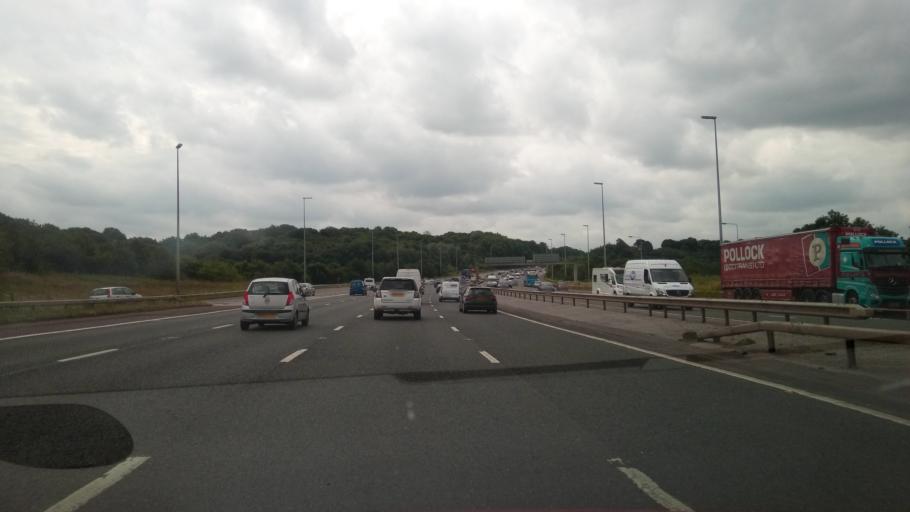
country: GB
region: England
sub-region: Lancashire
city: Goosnargh
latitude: 53.7633
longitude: -2.6356
